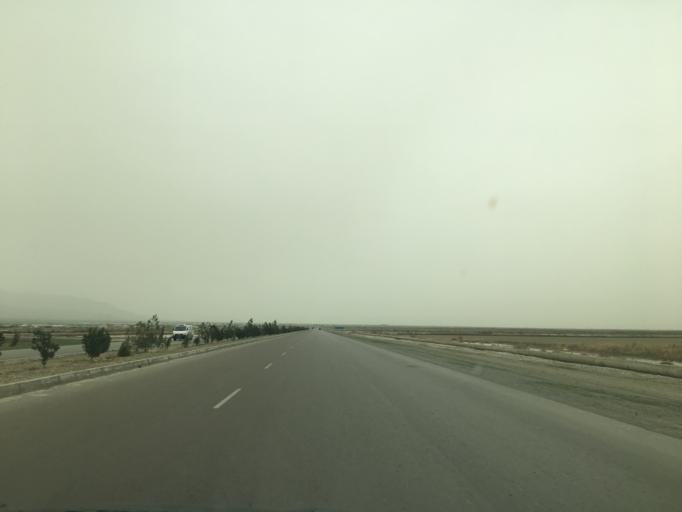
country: TM
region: Ahal
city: Baharly
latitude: 38.3714
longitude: 57.5162
